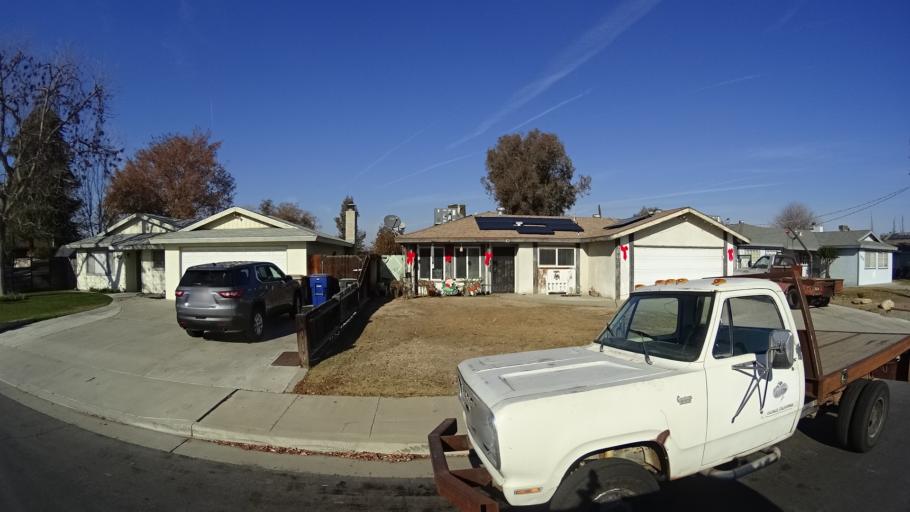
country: US
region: California
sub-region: Kern County
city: Greenfield
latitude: 35.3061
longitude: -119.0537
